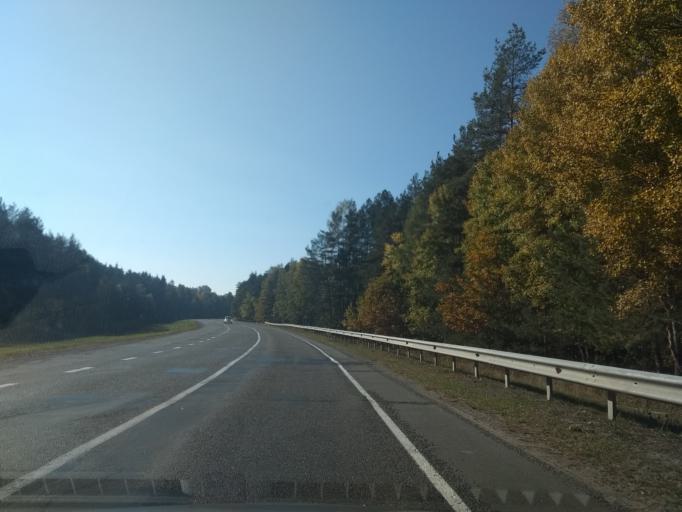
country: BY
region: Grodnenskaya
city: Zhyrovichy
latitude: 52.8583
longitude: 25.6544
